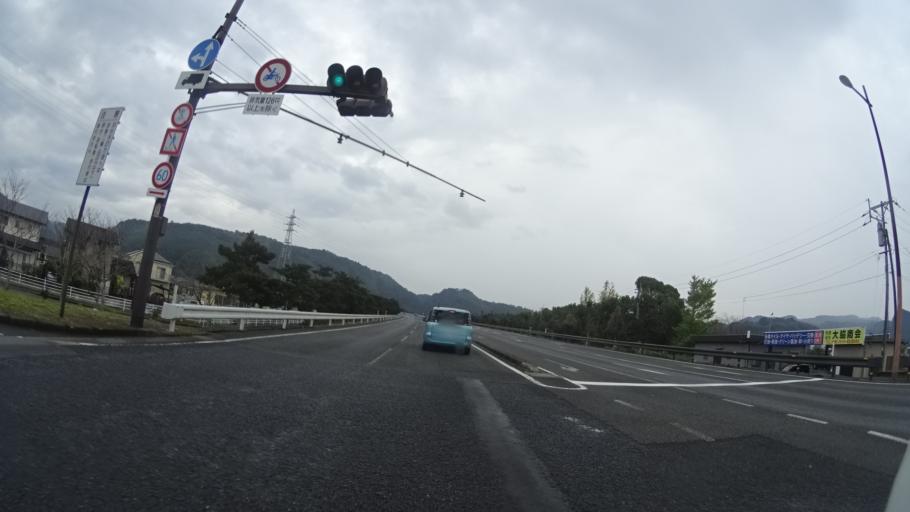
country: JP
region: Kagoshima
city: Kajiki
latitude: 31.7458
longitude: 130.6572
